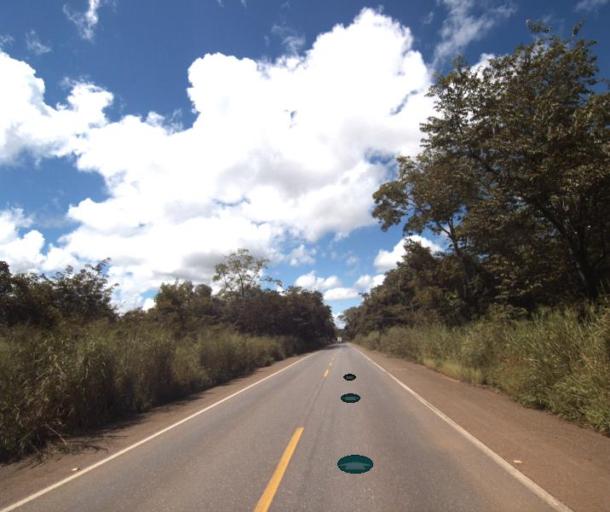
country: BR
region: Goias
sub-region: Petrolina De Goias
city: Petrolina de Goias
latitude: -15.9558
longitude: -49.1837
